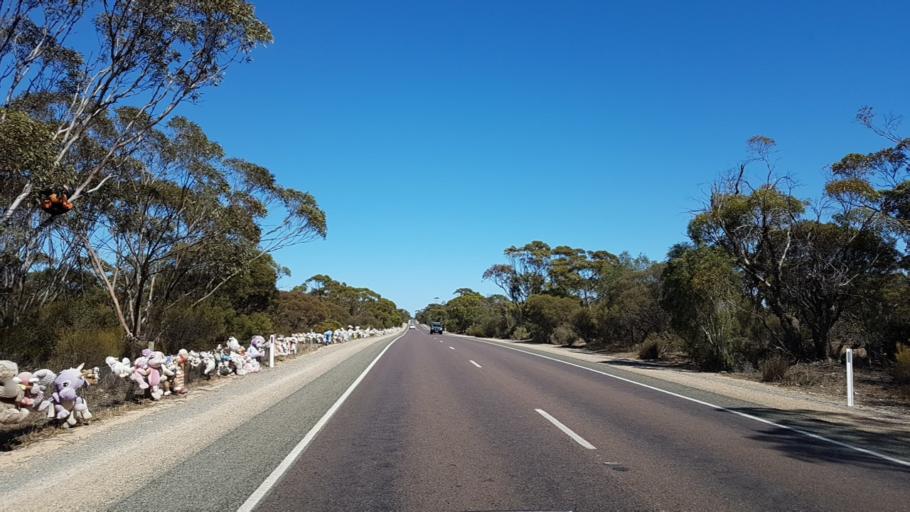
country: AU
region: South Australia
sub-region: Copper Coast
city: Kadina
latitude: -34.0498
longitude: 137.9751
